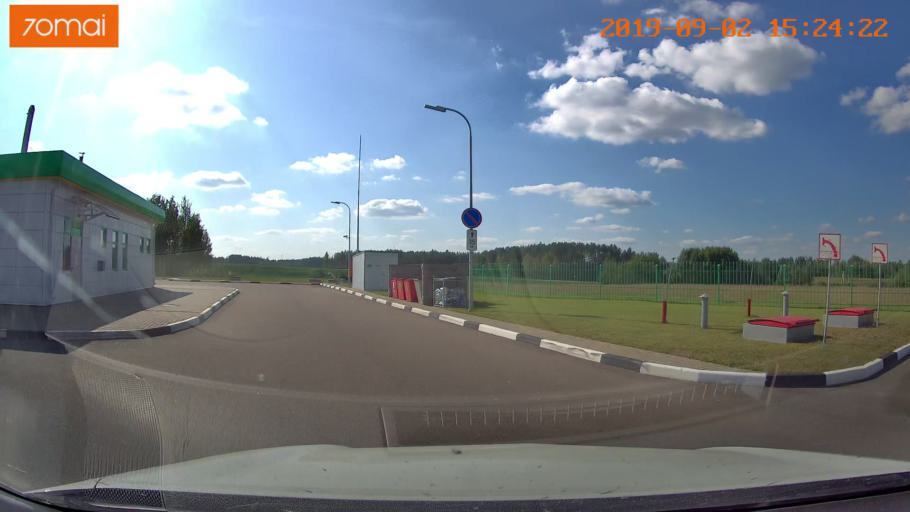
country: BY
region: Mogilev
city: Byalynichy
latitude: 53.9105
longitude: 29.4107
